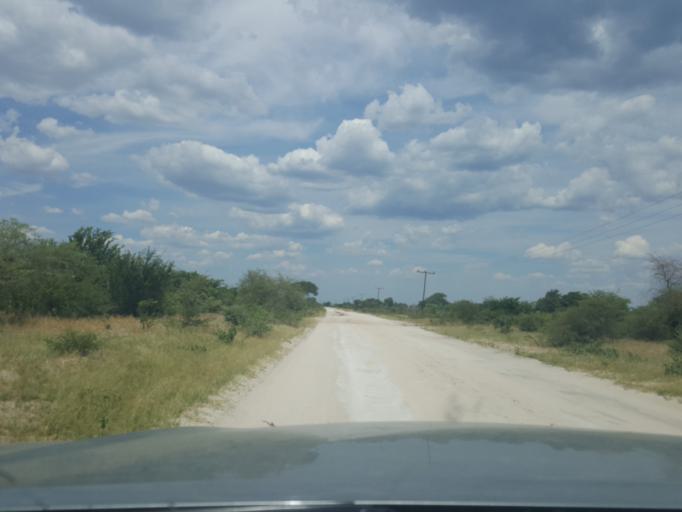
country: BW
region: North West
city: Shakawe
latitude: -18.5042
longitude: 22.1360
